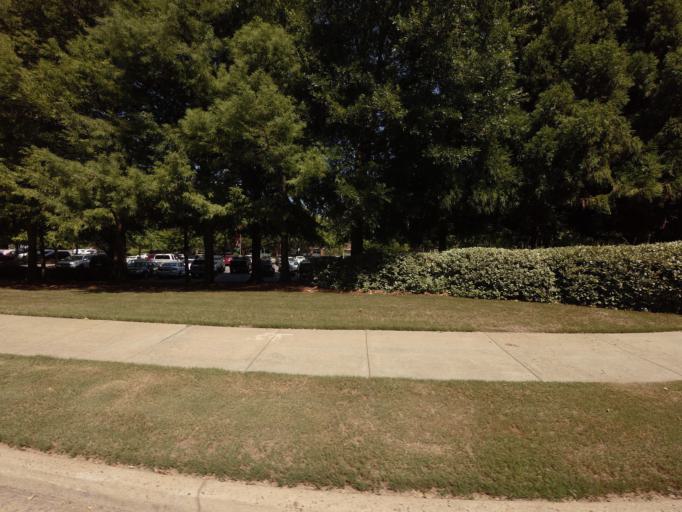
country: US
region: Georgia
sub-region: Fulton County
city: Johns Creek
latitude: 34.0577
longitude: -84.1709
